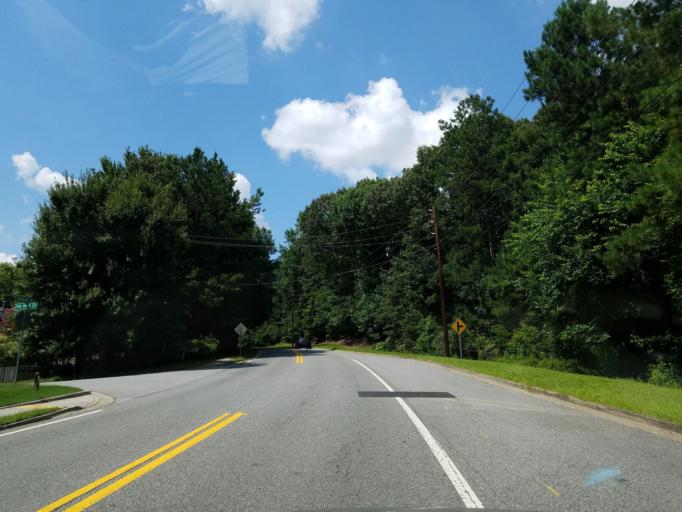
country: US
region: Georgia
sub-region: Fulton County
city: Roswell
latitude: 33.9949
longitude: -84.3340
